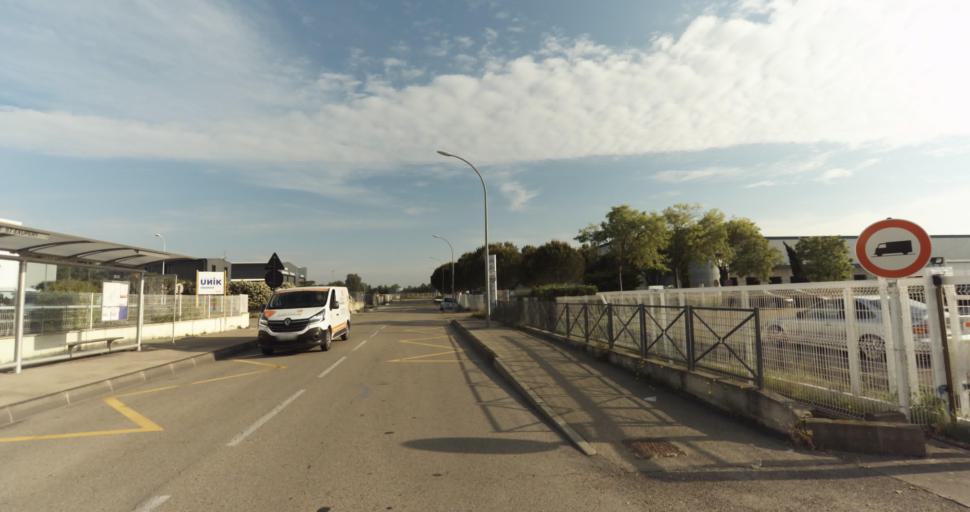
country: FR
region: Languedoc-Roussillon
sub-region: Departement du Gard
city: Rodilhan
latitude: 43.8384
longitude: 4.4217
